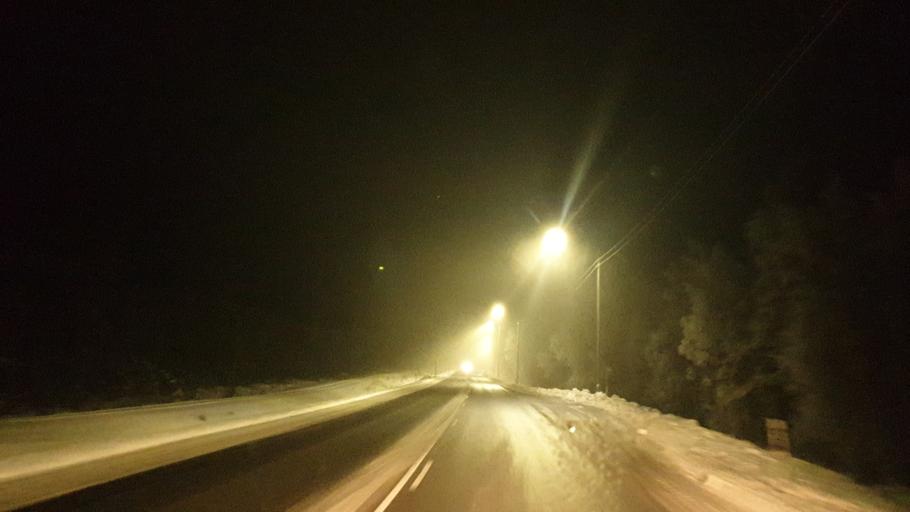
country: FI
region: Northern Ostrobothnia
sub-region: Oulunkaari
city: Kuivaniemi
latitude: 65.5218
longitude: 25.2655
